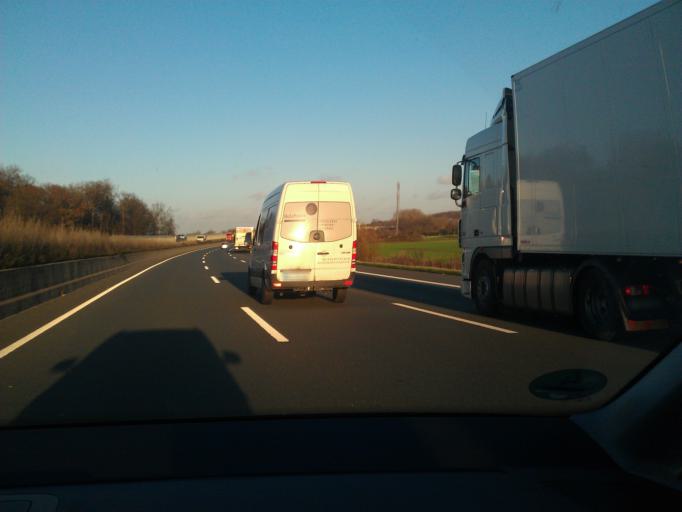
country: DE
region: North Rhine-Westphalia
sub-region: Regierungsbezirk Munster
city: Beckum
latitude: 51.7711
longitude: 8.0094
